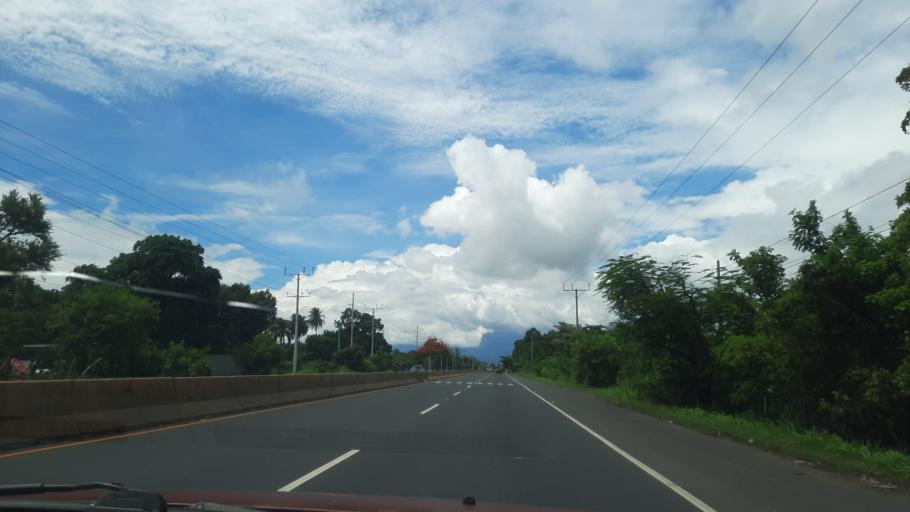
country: SV
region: Sonsonate
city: San Antonio del Monte
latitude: 13.6504
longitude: -89.7674
